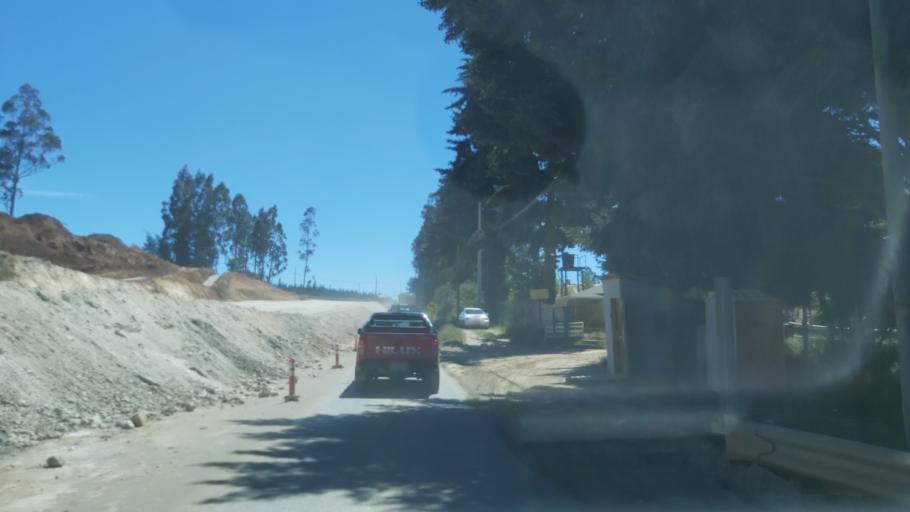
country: CL
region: Maule
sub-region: Provincia de Talca
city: Constitucion
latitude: -35.3868
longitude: -72.4222
